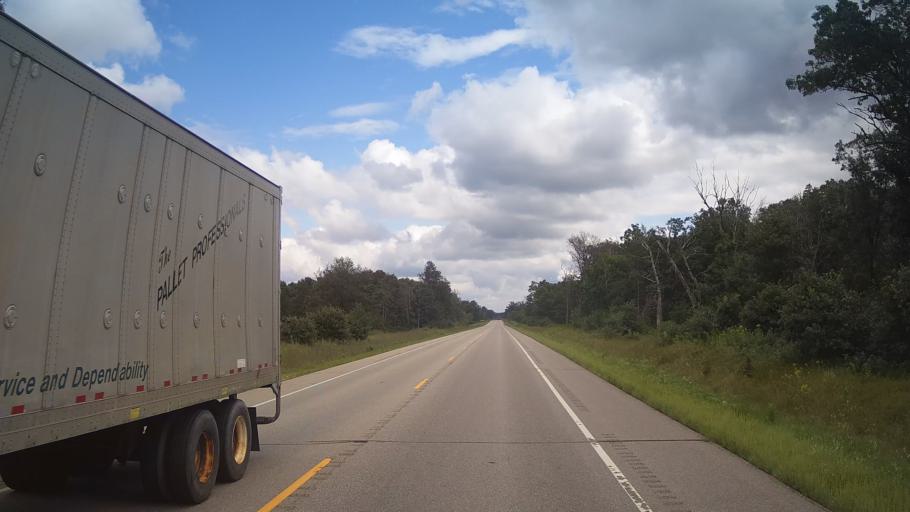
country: US
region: Wisconsin
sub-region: Adams County
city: Friendship
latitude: 44.0255
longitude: -89.7138
